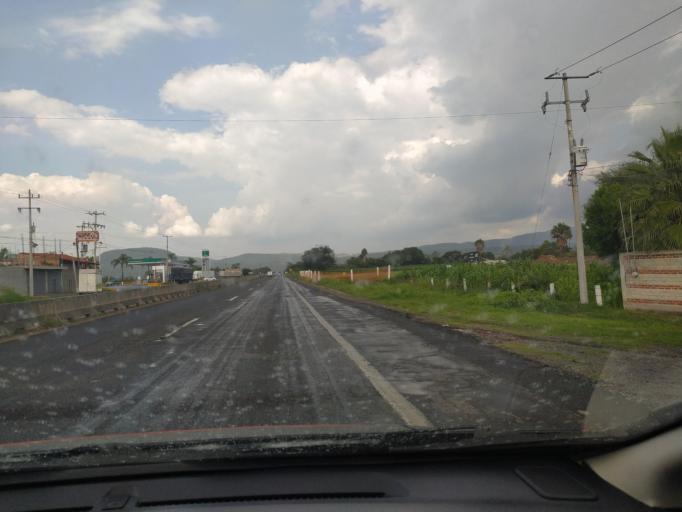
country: MX
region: Jalisco
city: Bellavista
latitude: 20.4173
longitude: -103.6245
